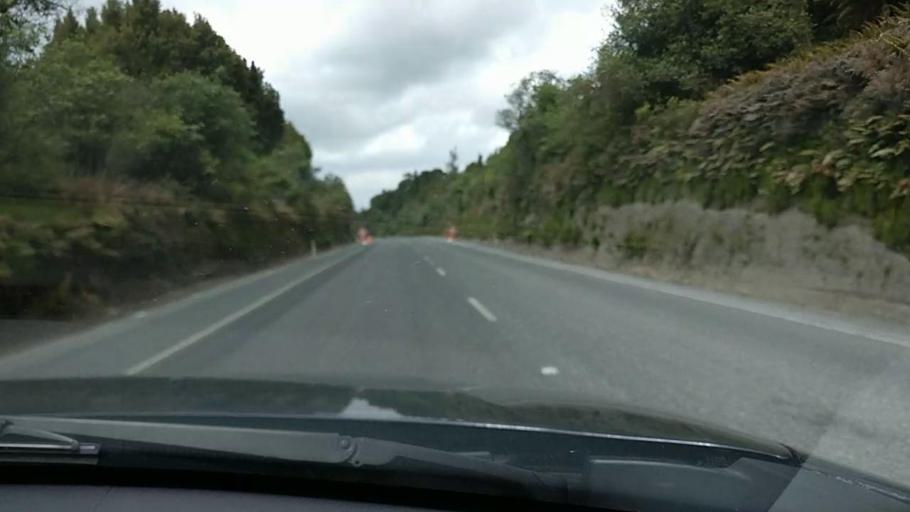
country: NZ
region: Bay of Plenty
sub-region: Rotorua District
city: Rotorua
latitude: -38.0680
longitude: 176.1097
